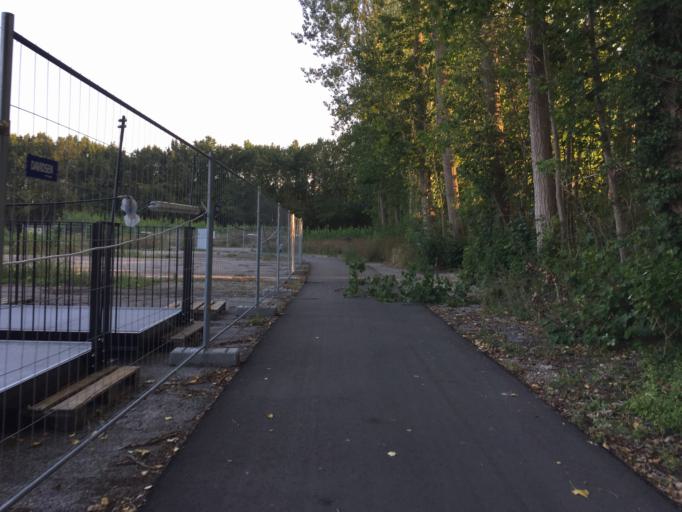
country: DK
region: South Denmark
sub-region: Odense Kommune
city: Odense
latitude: 55.3719
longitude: 10.4040
